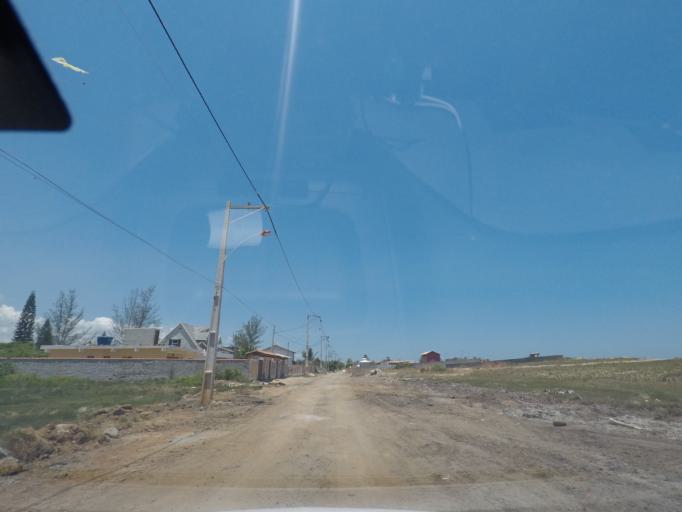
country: BR
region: Rio de Janeiro
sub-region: Niteroi
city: Niteroi
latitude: -22.9685
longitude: -42.9719
